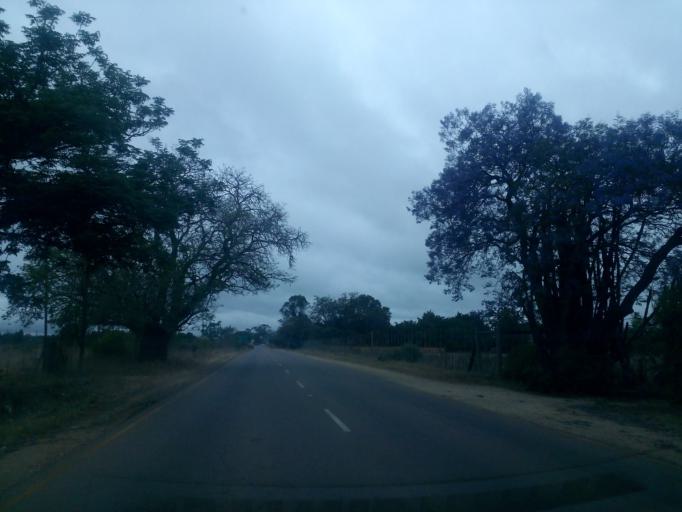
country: ZA
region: Limpopo
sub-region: Vhembe District Municipality
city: Louis Trichardt
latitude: -23.0787
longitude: 29.9036
